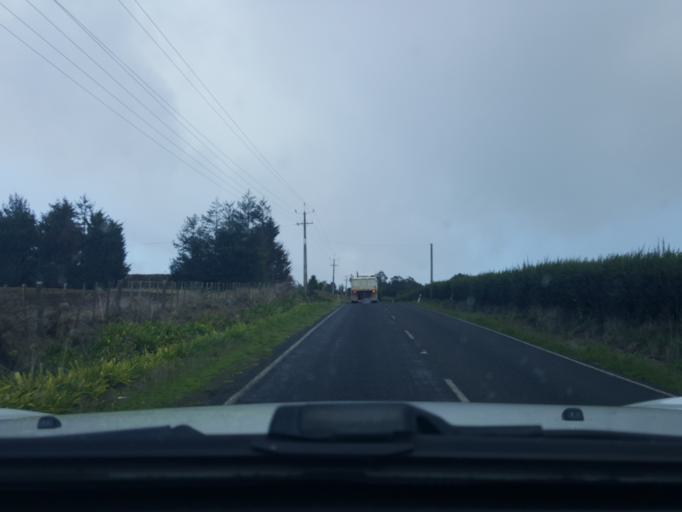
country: NZ
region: Auckland
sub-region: Auckland
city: Pukekohe East
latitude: -37.3081
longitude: 174.9961
